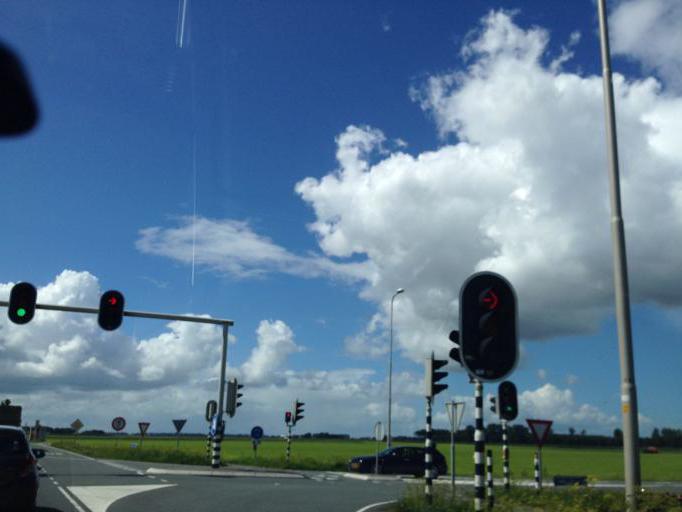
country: NL
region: Flevoland
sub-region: Gemeente Noordoostpolder
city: Ens
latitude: 52.5455
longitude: 5.8153
